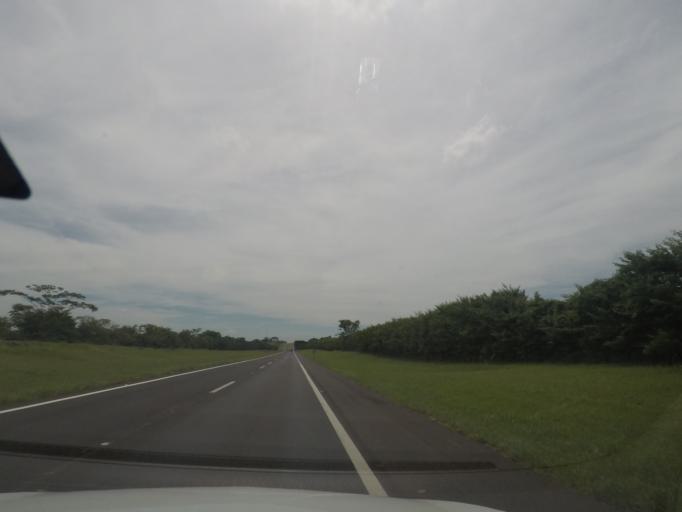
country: BR
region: Sao Paulo
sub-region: Bebedouro
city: Bebedouro
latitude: -20.9786
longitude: -48.4375
